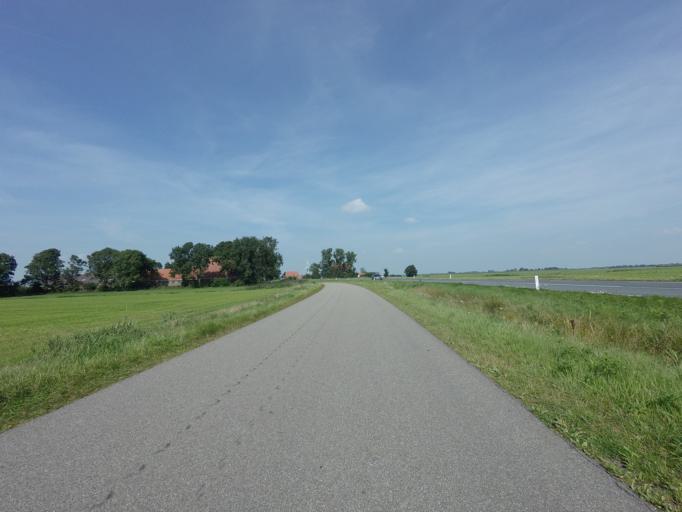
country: NL
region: Friesland
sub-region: Sudwest Fryslan
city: Woudsend
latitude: 52.9468
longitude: 5.6536
